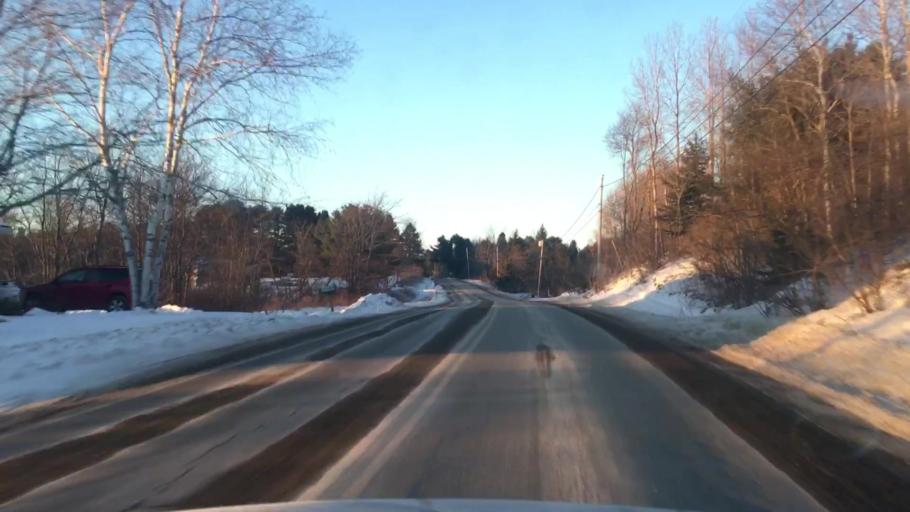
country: US
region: Maine
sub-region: Penobscot County
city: Brewer
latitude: 44.7406
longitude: -68.7651
